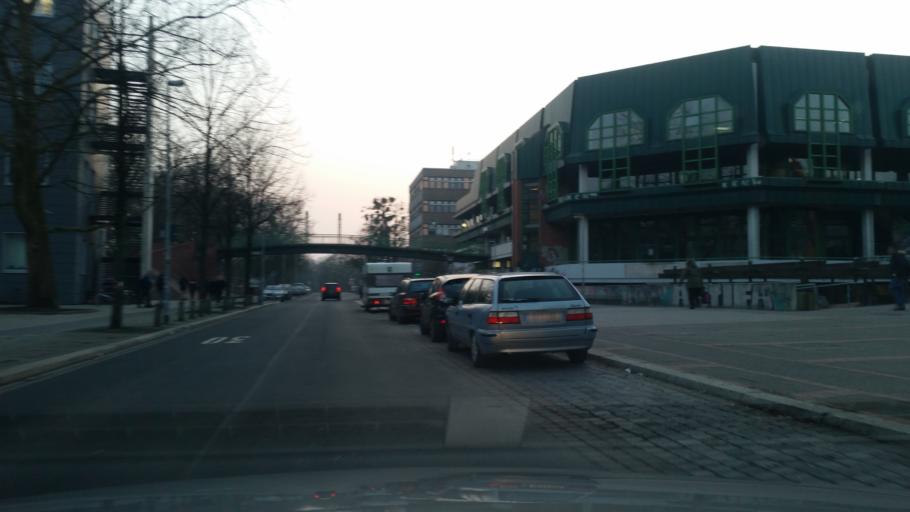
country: DE
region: Lower Saxony
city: Hannover
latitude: 52.3866
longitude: 9.7152
